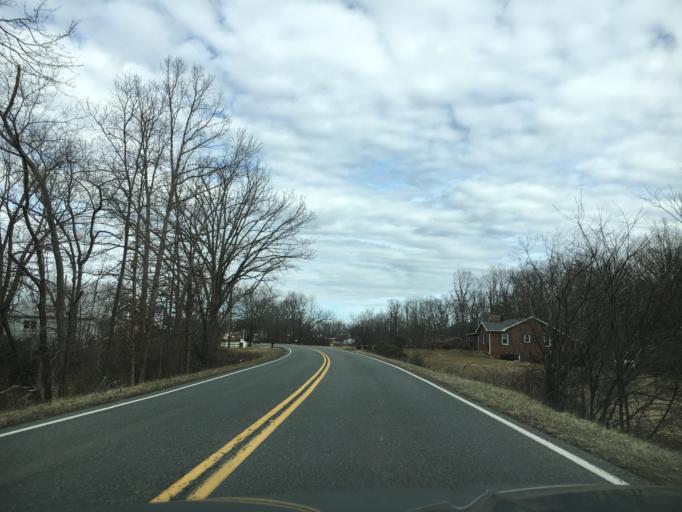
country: US
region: Virginia
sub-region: Augusta County
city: Dooms
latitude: 38.1283
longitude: -78.8465
